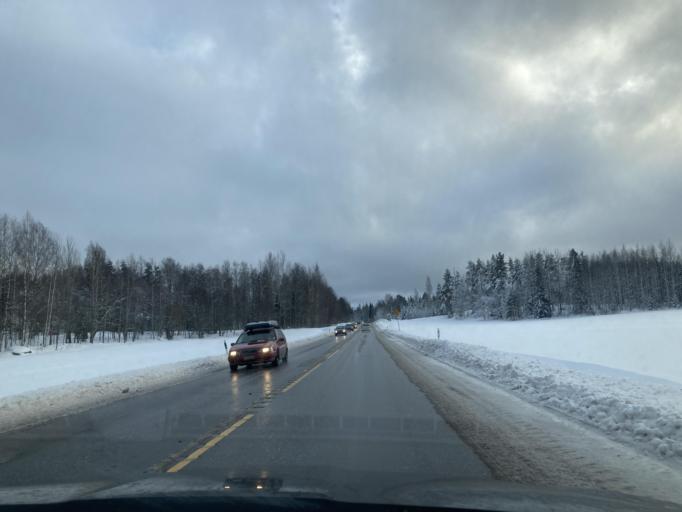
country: FI
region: Paijanne Tavastia
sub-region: Lahti
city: Padasjoki
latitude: 61.3134
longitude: 25.2909
